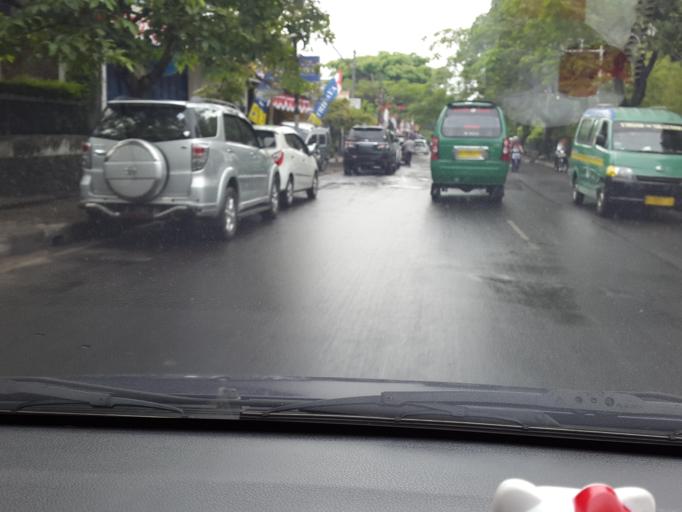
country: ID
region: West Java
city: Bandung
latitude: -6.9047
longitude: 107.6314
